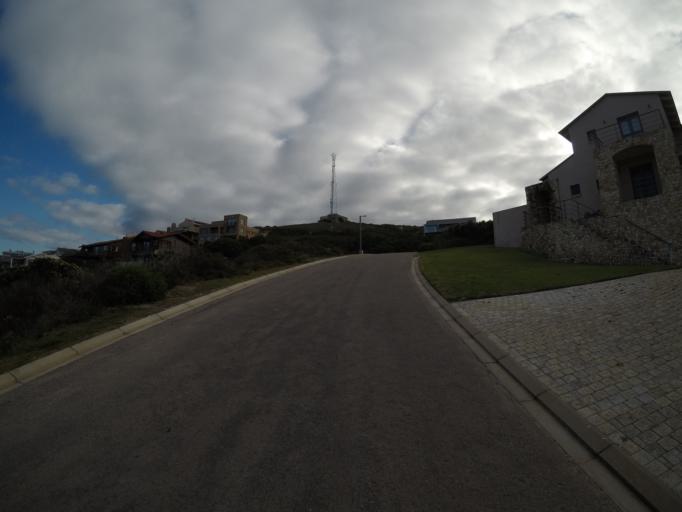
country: ZA
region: Western Cape
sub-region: Eden District Municipality
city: Riversdale
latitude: -34.4294
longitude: 21.3335
